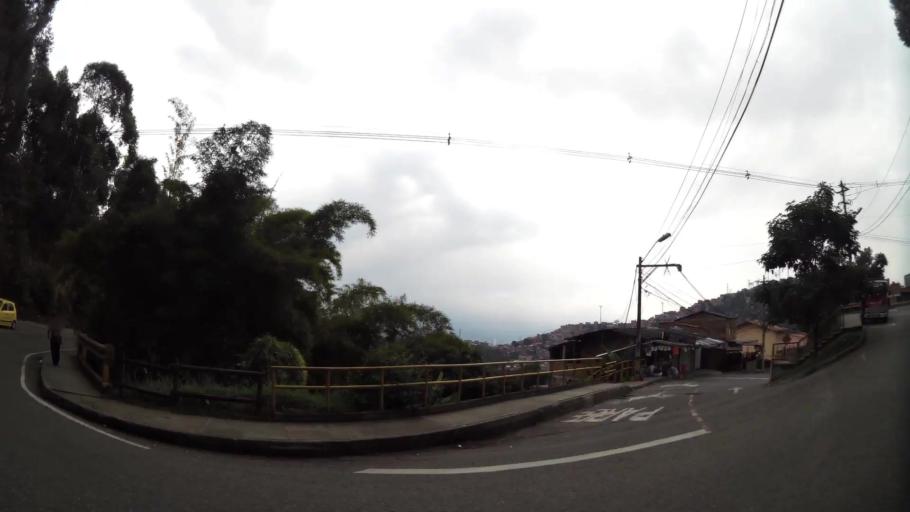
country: CO
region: Antioquia
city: Medellin
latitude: 6.2774
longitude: -75.6173
